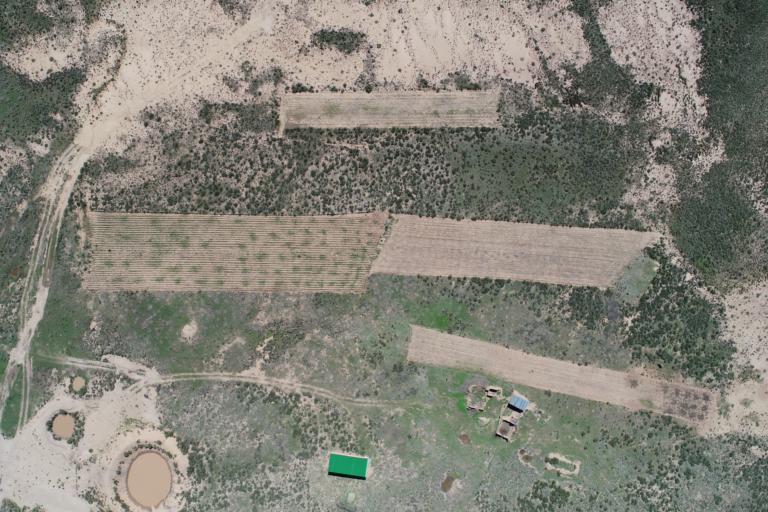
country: BO
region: La Paz
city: Patacamaya
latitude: -17.2901
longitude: -68.4865
